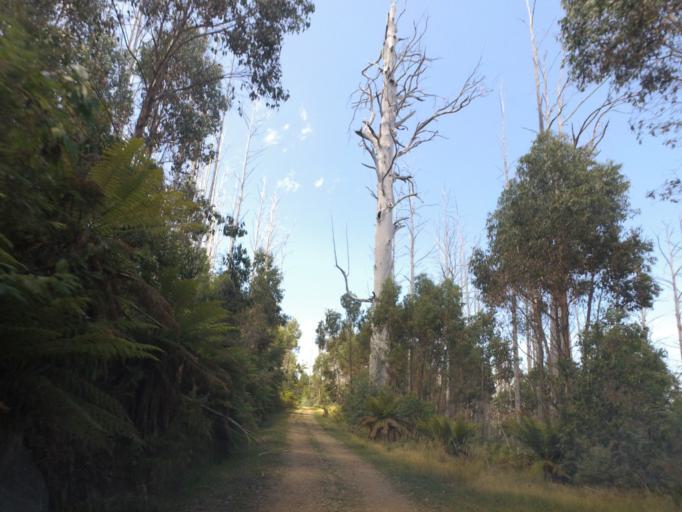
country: AU
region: Victoria
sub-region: Murrindindi
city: Alexandra
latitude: -37.4783
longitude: 145.8355
